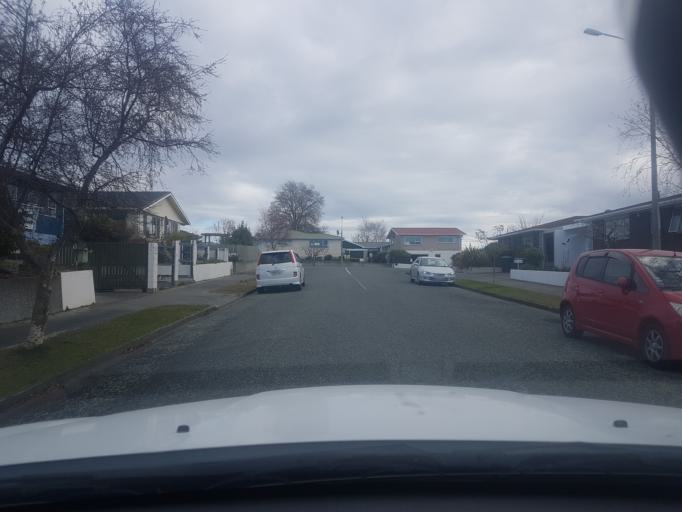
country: NZ
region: Canterbury
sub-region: Timaru District
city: Timaru
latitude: -44.3888
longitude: 171.2024
